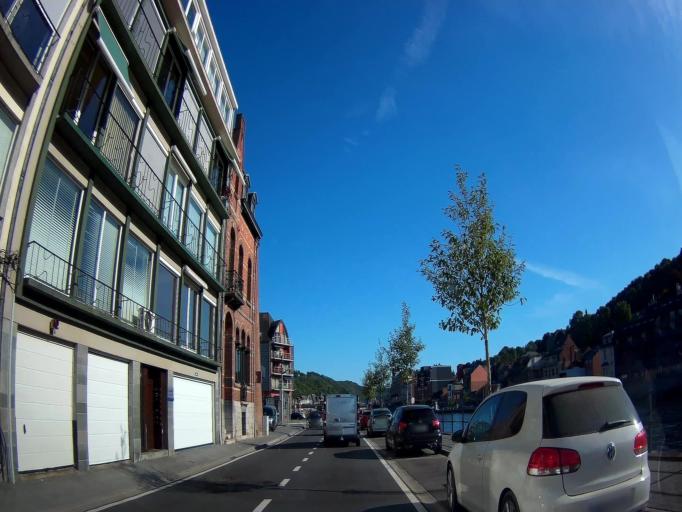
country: BE
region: Wallonia
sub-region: Province de Namur
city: Dinant
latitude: 50.2633
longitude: 4.9085
